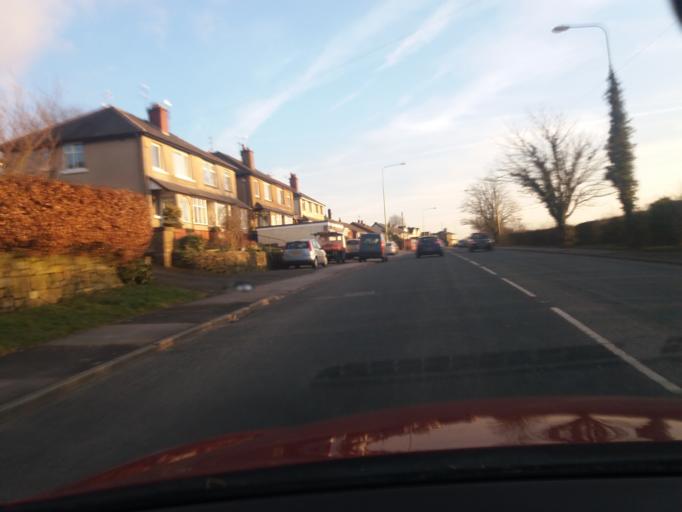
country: GB
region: England
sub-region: Lancashire
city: Chorley
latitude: 53.6738
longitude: -2.6158
